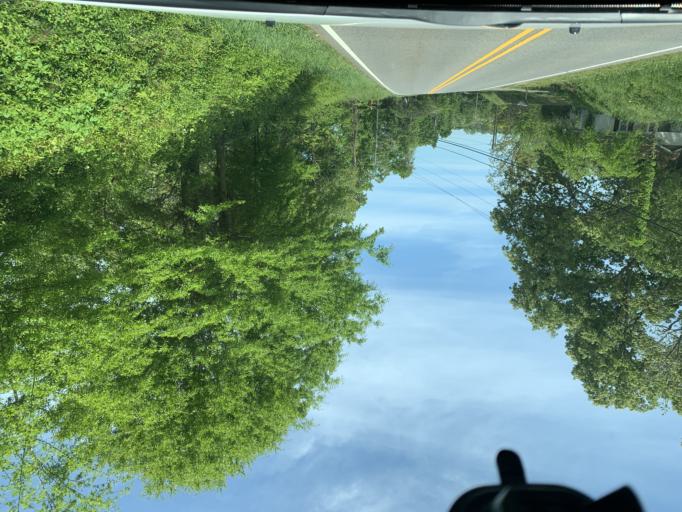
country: US
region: Georgia
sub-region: Forsyth County
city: Cumming
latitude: 34.2691
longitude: -84.1749
